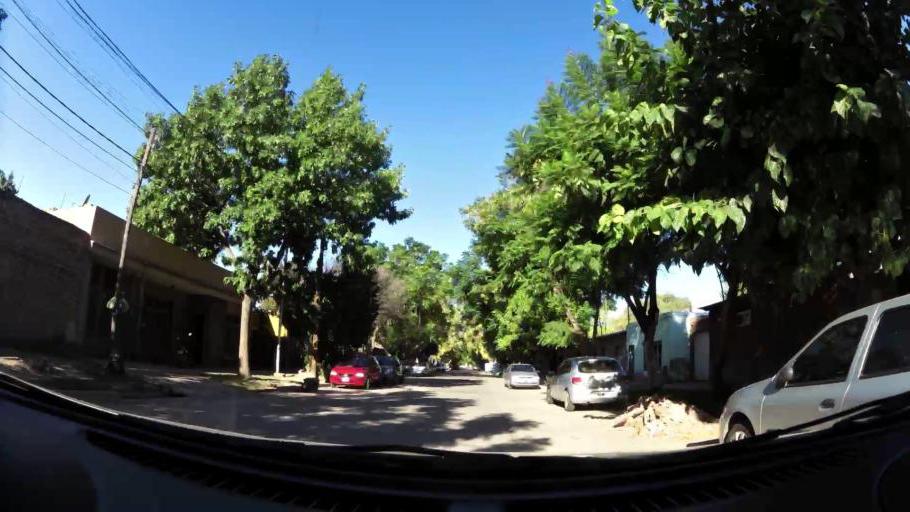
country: AR
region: Mendoza
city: Las Heras
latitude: -32.8430
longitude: -68.8261
